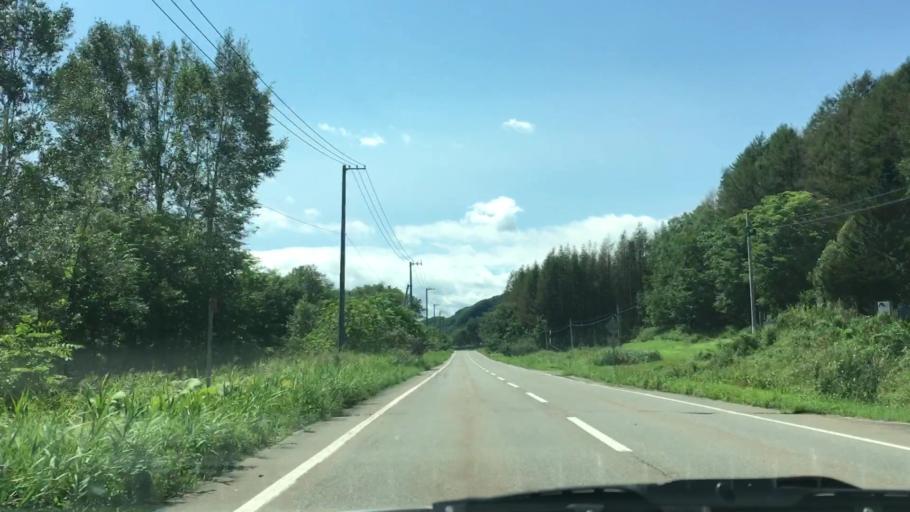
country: JP
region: Hokkaido
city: Otofuke
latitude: 43.2638
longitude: 143.5797
